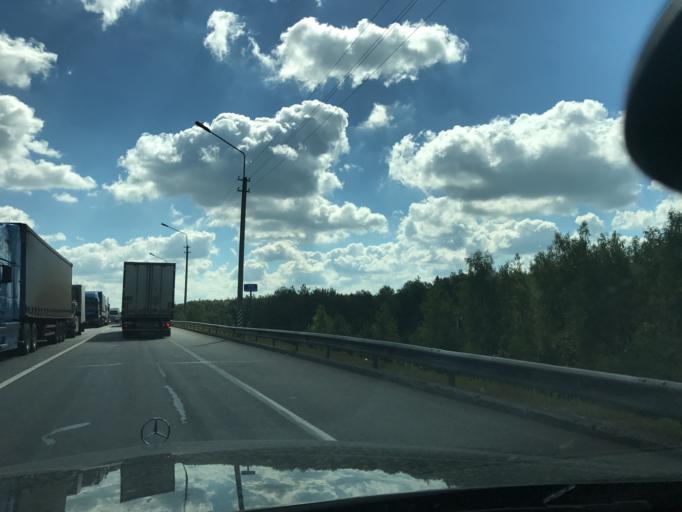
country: RU
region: Vladimir
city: Vorsha
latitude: 56.0763
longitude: 40.2113
